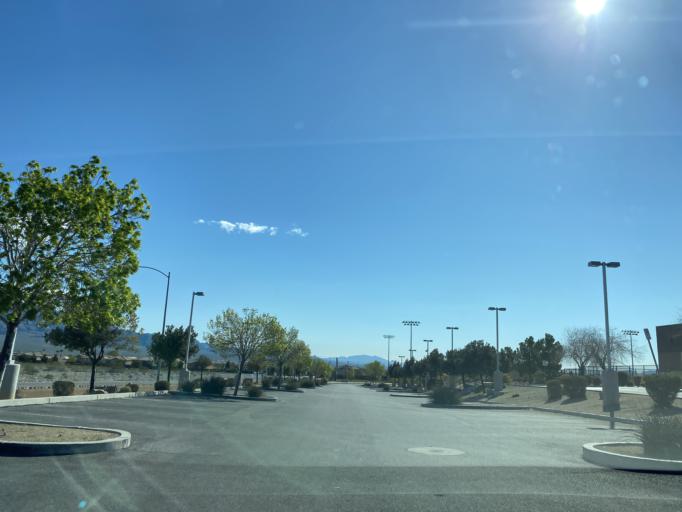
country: US
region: Nevada
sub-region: Clark County
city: Summerlin South
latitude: 36.3212
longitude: -115.3000
